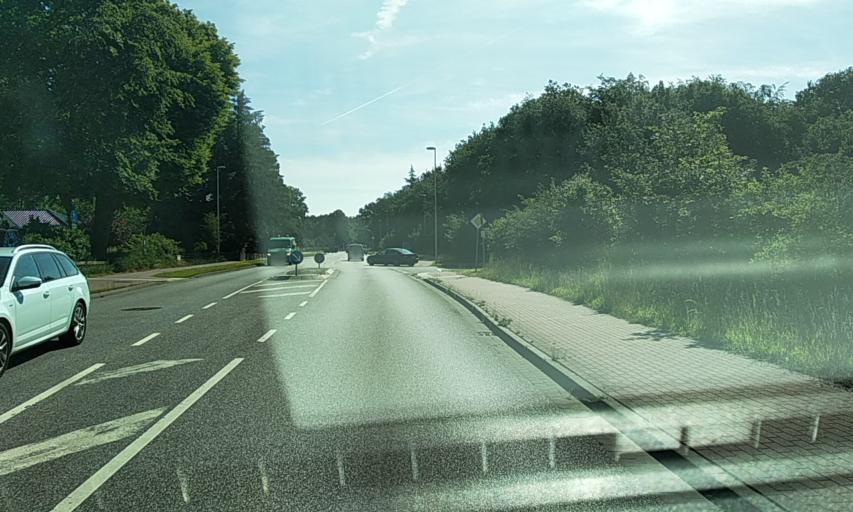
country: DE
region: Schleswig-Holstein
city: Fockbek
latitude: 54.3095
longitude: 9.6181
